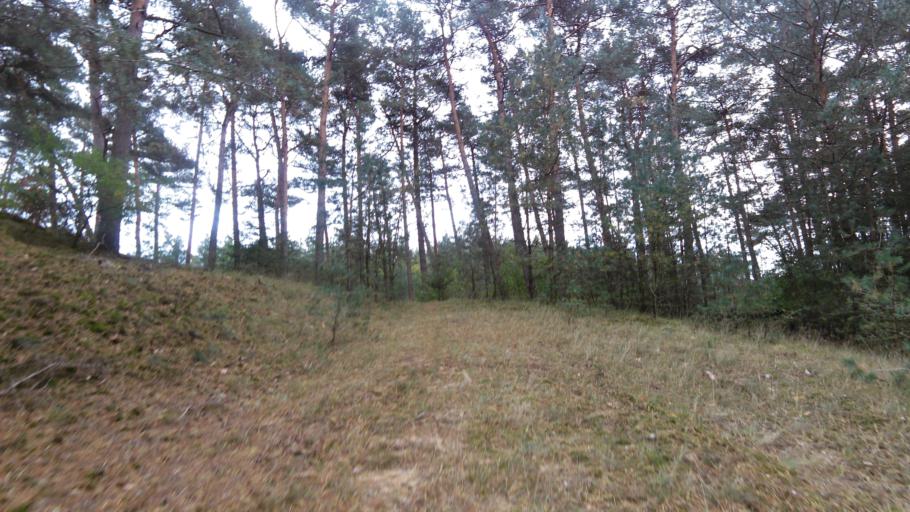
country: NL
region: Gelderland
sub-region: Gemeente Ede
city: Harskamp
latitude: 52.1619
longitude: 5.7865
